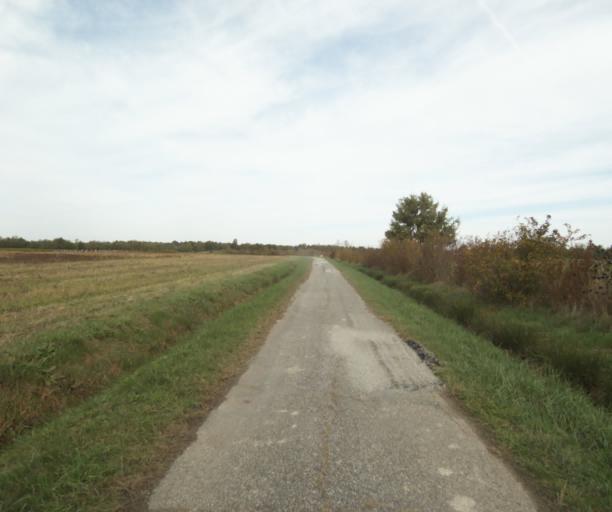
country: FR
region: Midi-Pyrenees
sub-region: Departement de la Haute-Garonne
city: Fronton
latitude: 43.8750
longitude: 1.3889
